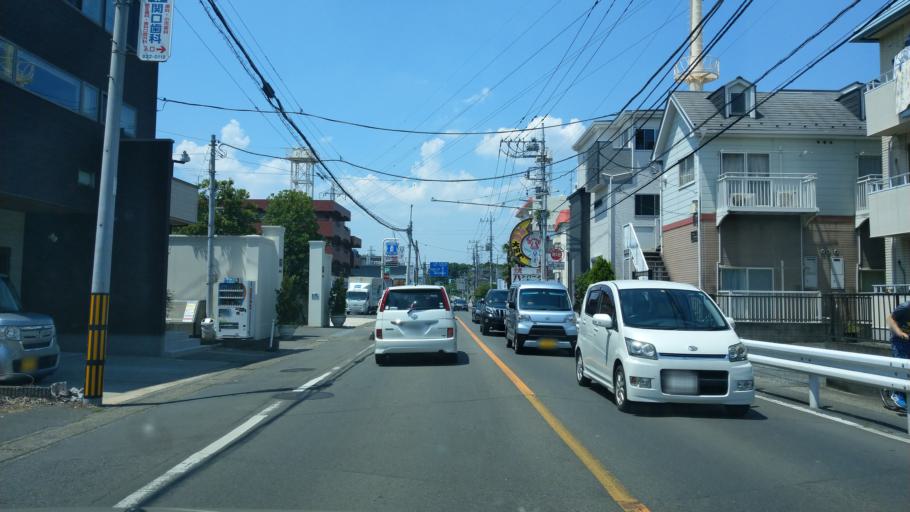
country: JP
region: Saitama
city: Yono
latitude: 35.8888
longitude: 139.6450
